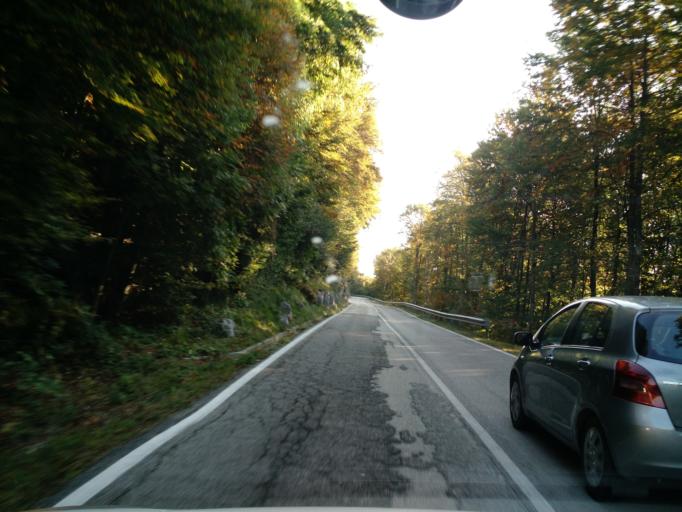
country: IT
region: Veneto
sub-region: Provincia di Vicenza
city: Lusiana
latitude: 45.8085
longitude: 11.5731
